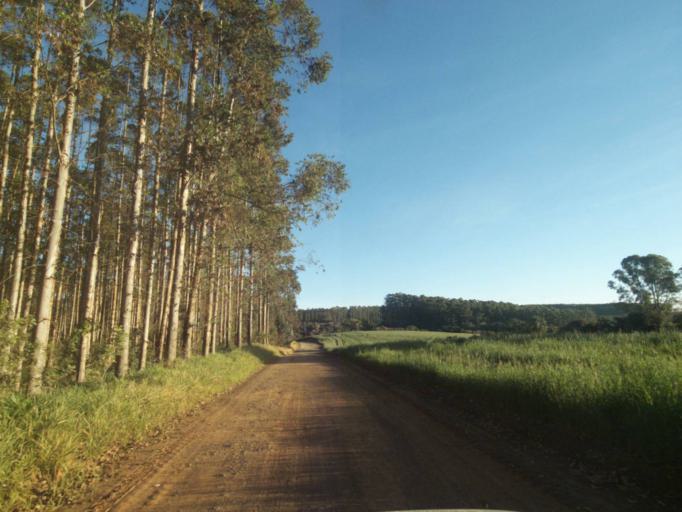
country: BR
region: Parana
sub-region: Telemaco Borba
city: Telemaco Borba
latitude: -24.4873
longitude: -50.5934
